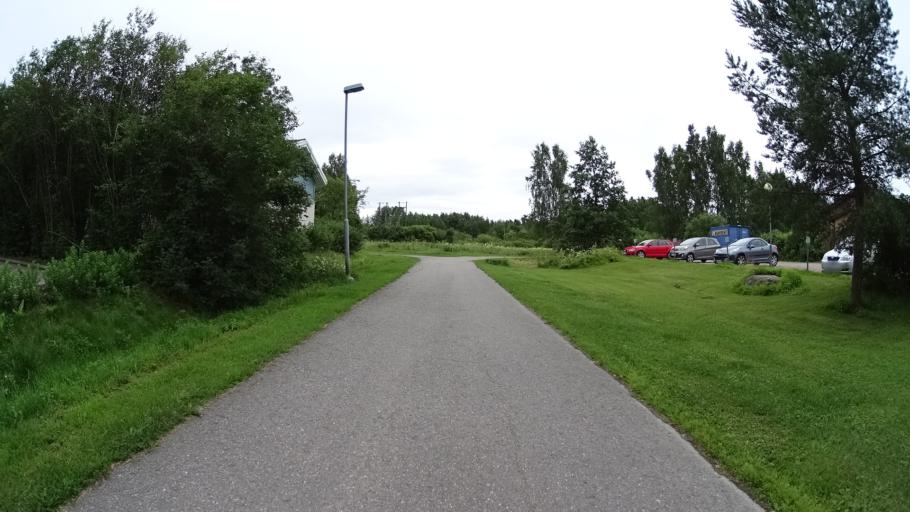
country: FI
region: Uusimaa
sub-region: Helsinki
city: Kauniainen
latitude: 60.2395
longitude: 24.7162
